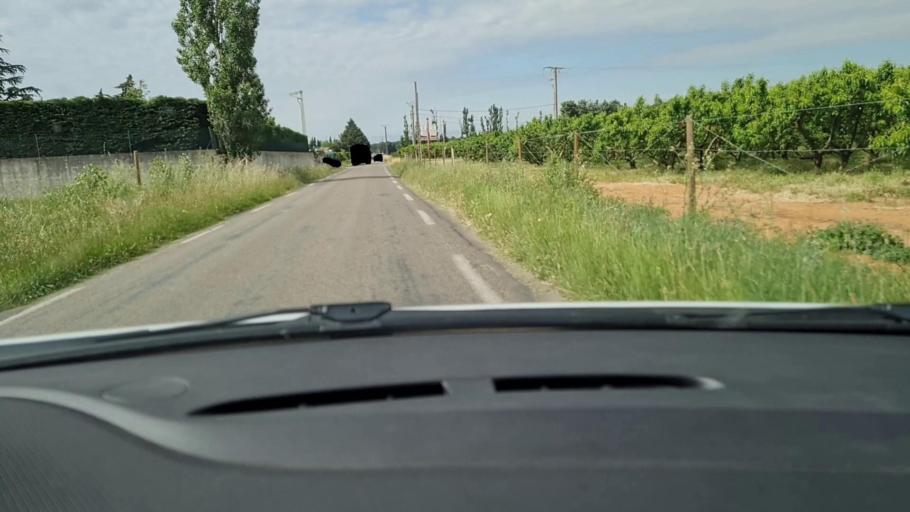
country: FR
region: Languedoc-Roussillon
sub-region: Departement du Gard
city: Jonquieres-Saint-Vincent
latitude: 43.8049
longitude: 4.5410
